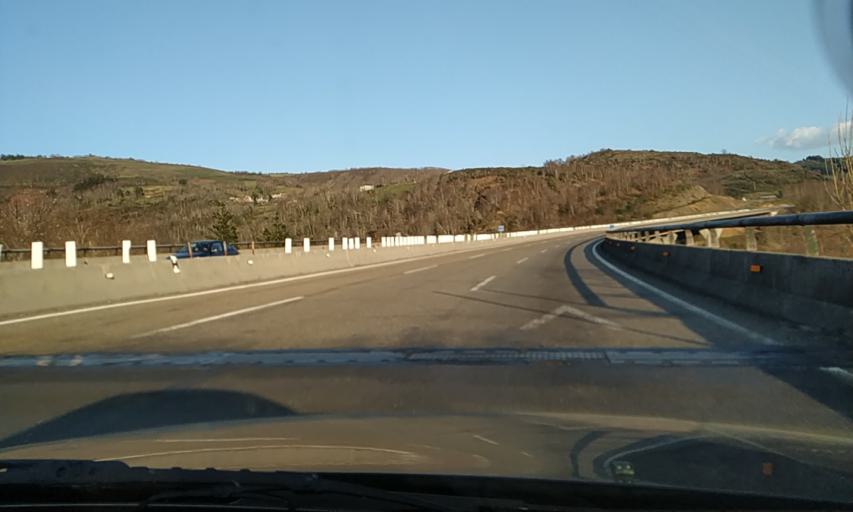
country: ES
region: Galicia
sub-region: Provincia de Lugo
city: San Roman
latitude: 42.7500
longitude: -7.0609
